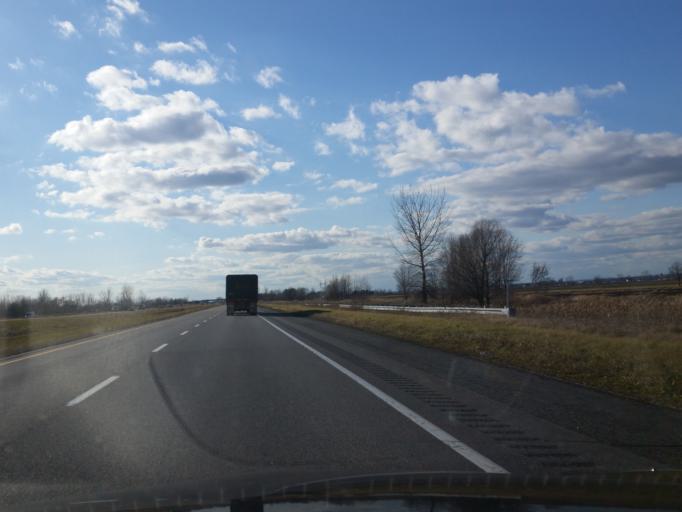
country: CA
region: Quebec
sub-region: Mauricie
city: Maskinonge
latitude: 46.1673
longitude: -73.0692
